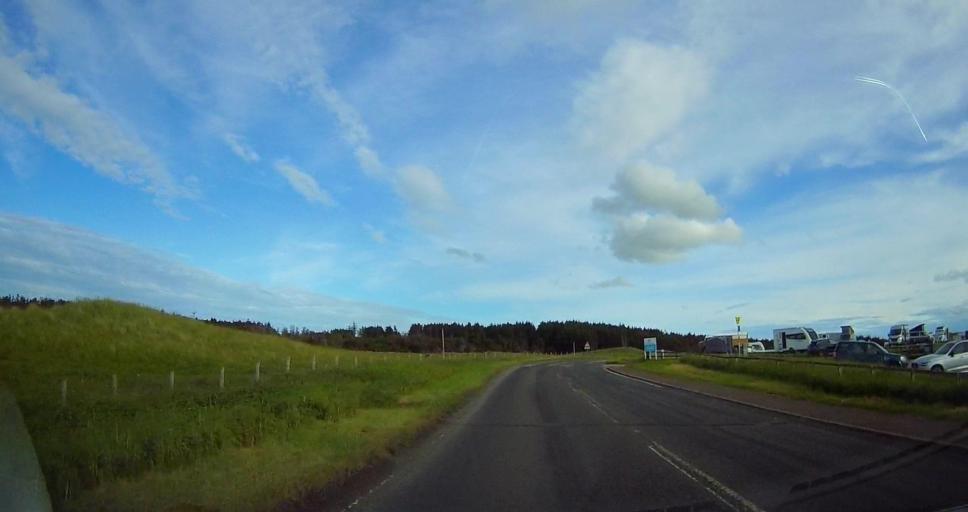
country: GB
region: Scotland
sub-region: Highland
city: Thurso
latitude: 58.6162
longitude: -3.3456
